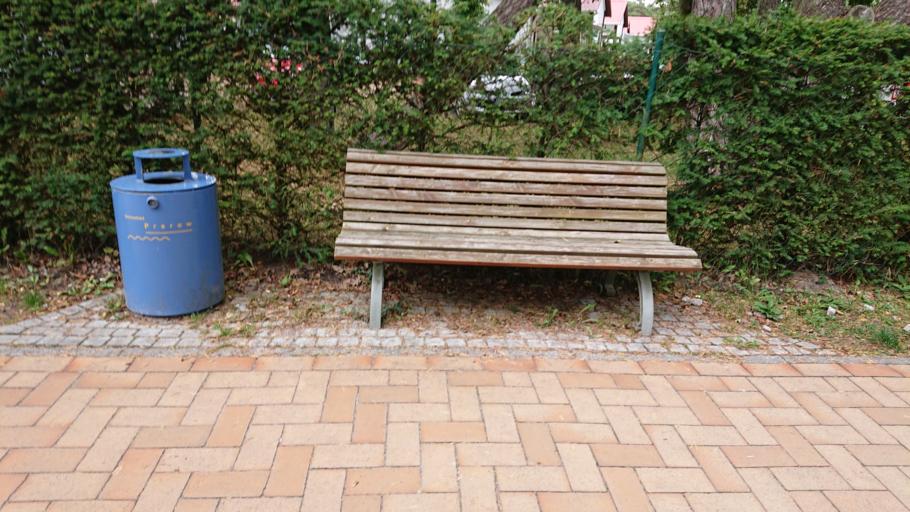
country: DE
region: Mecklenburg-Vorpommern
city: Ostseebad Prerow
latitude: 54.4529
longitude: 12.5546
